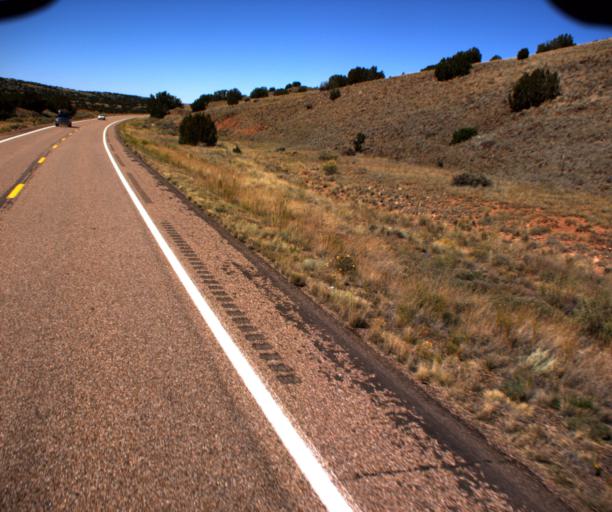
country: US
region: Arizona
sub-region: Apache County
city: Saint Johns
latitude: 34.5715
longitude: -109.5235
